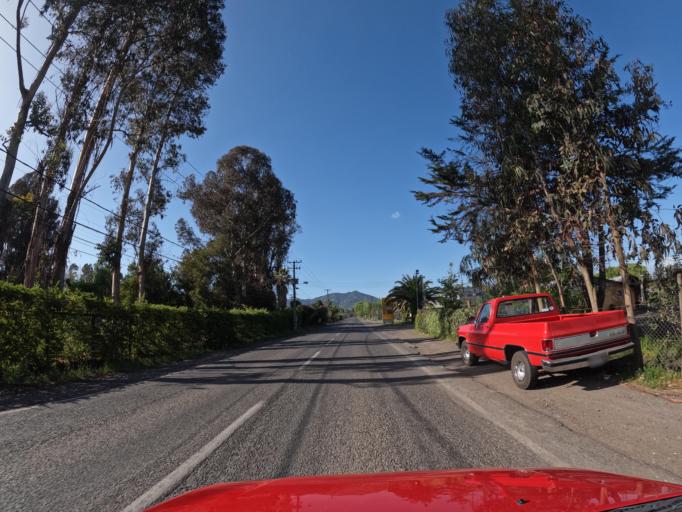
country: CL
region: Maule
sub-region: Provincia de Curico
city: Rauco
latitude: -34.8724
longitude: -71.2662
